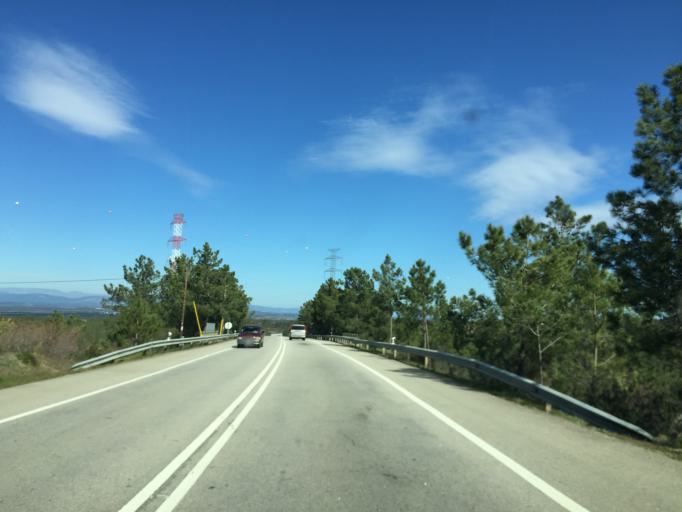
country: PT
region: Castelo Branco
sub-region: Castelo Branco
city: Castelo Branco
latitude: 39.7713
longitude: -7.5870
